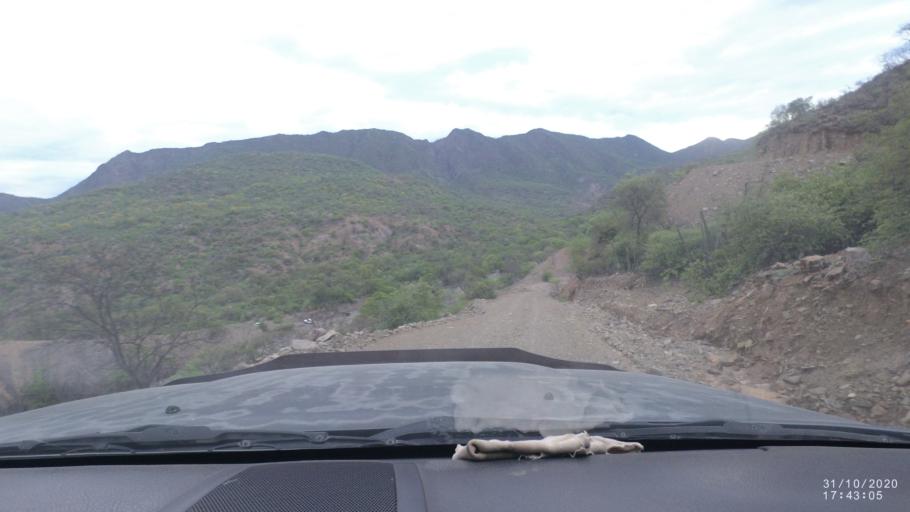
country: BO
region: Chuquisaca
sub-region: Provincia Zudanez
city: Mojocoya
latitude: -18.6096
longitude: -64.5463
